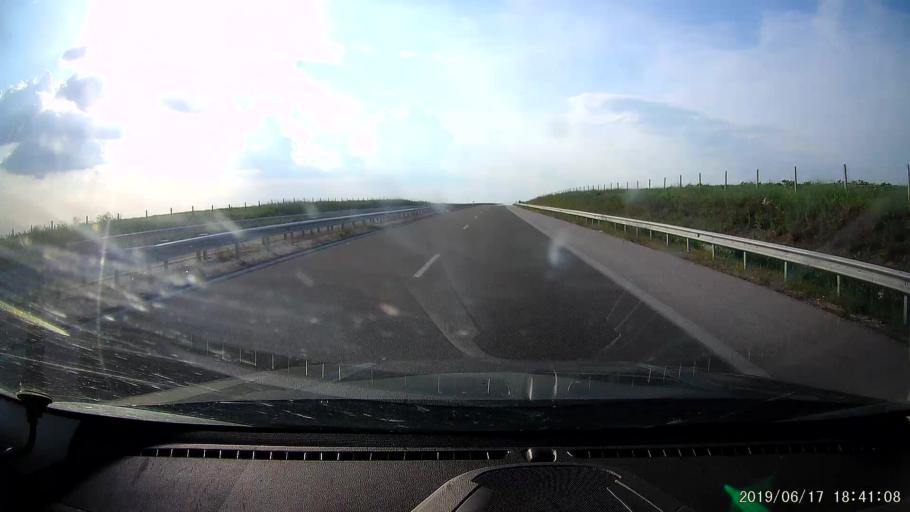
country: BG
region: Stara Zagora
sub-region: Obshtina Chirpan
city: Chirpan
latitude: 42.1665
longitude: 25.2614
